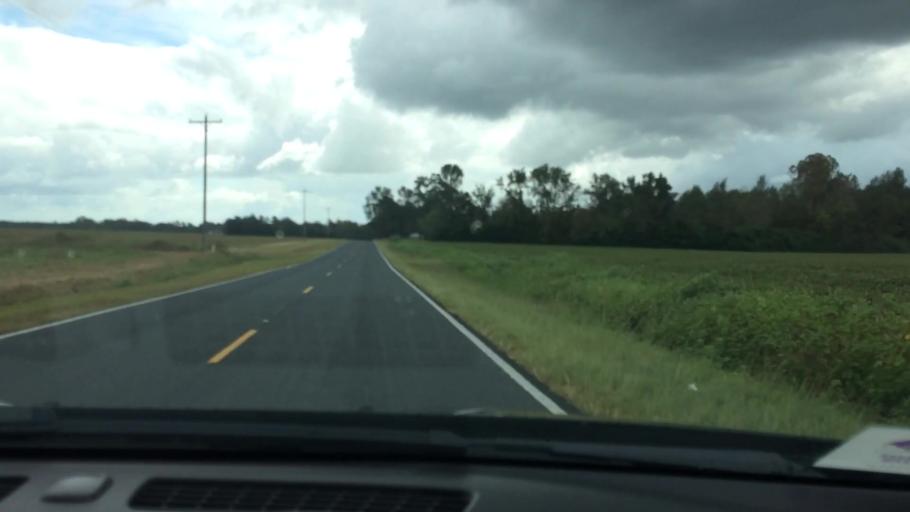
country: US
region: North Carolina
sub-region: Greene County
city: Maury
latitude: 35.5069
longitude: -77.5252
